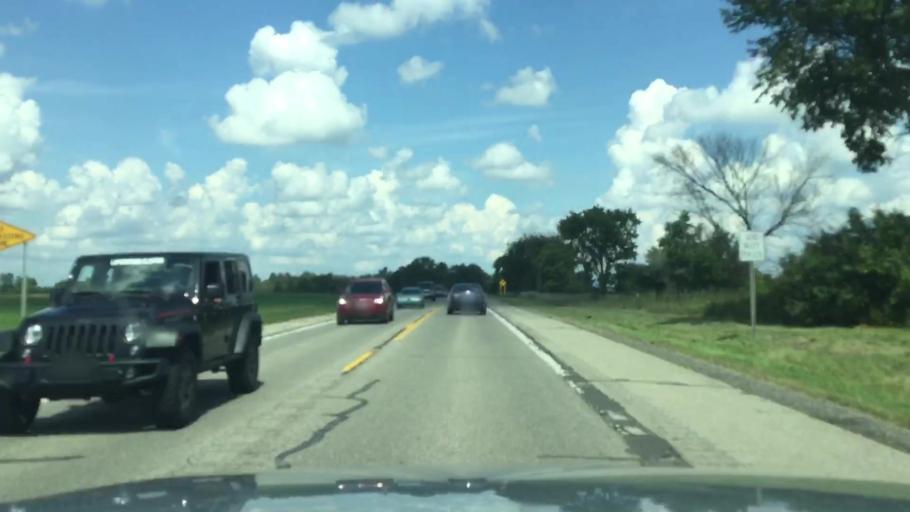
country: US
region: Michigan
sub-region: Lenawee County
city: Clinton
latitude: 42.1029
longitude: -83.8976
